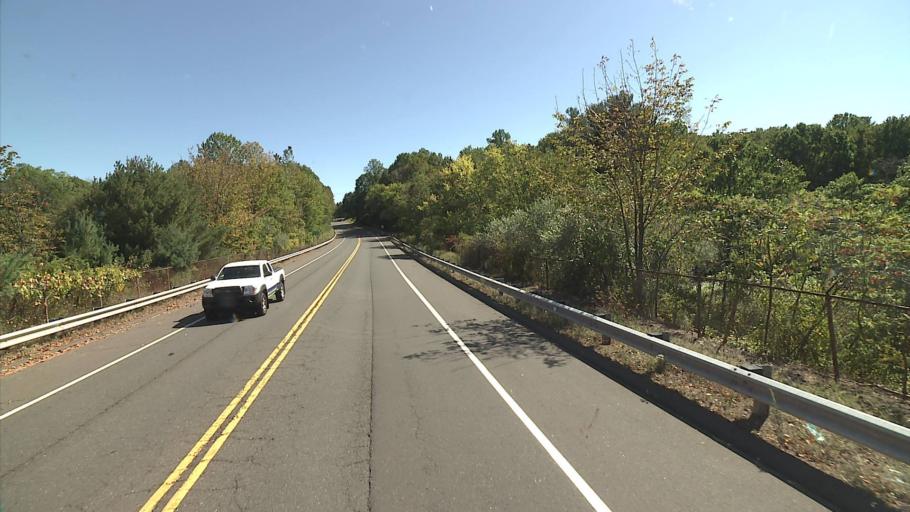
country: US
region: Connecticut
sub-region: New Haven County
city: Cheshire Village
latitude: 41.4957
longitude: -72.8556
